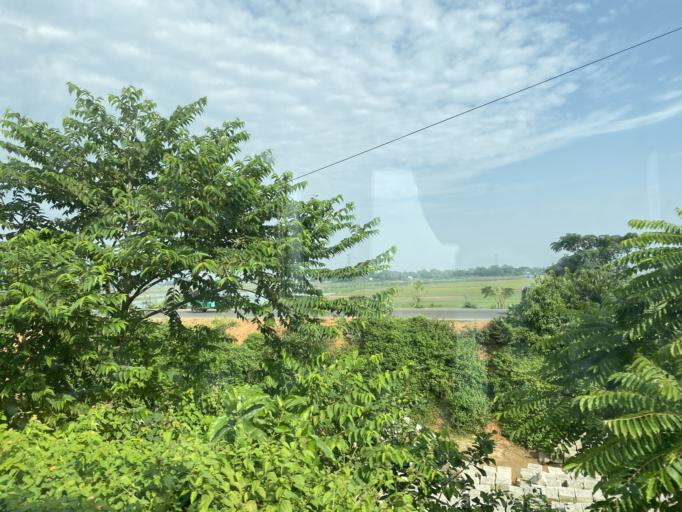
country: IN
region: Tripura
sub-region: West Tripura
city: Agartala
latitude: 23.8795
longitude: 91.2014
